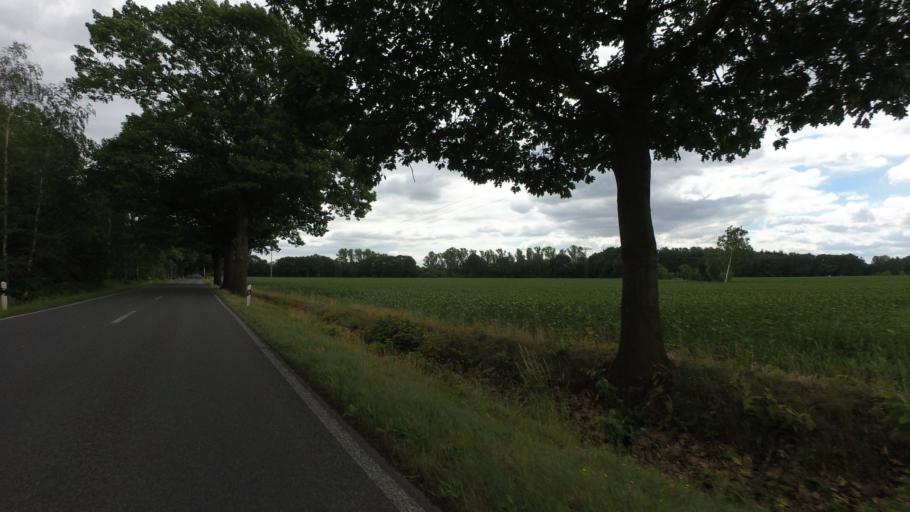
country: DE
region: Brandenburg
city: Calau
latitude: 51.7953
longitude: 13.8605
